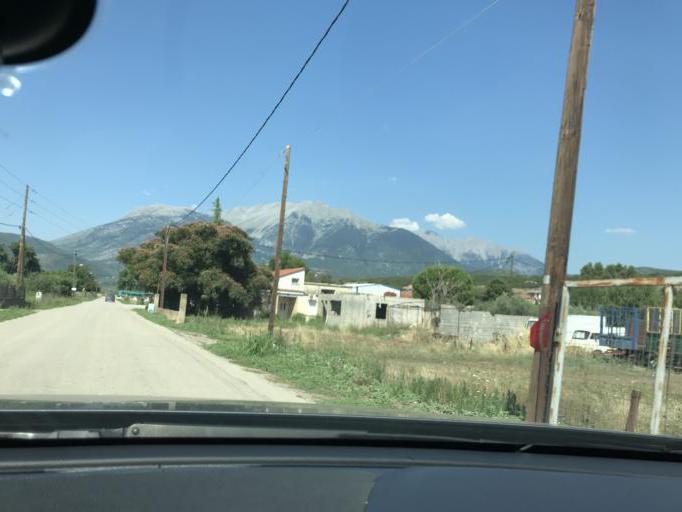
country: GR
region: Central Greece
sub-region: Nomos Fthiotidos
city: Elateia
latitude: 38.5236
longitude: 22.7852
